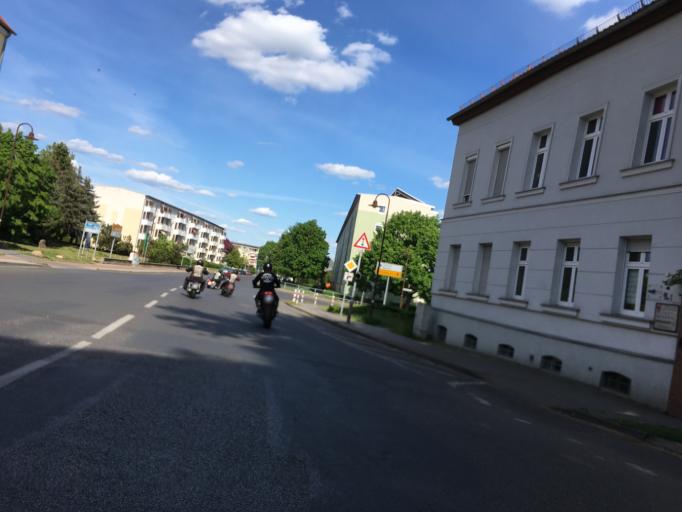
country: DE
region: Brandenburg
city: Wriezen
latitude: 52.7148
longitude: 14.1321
